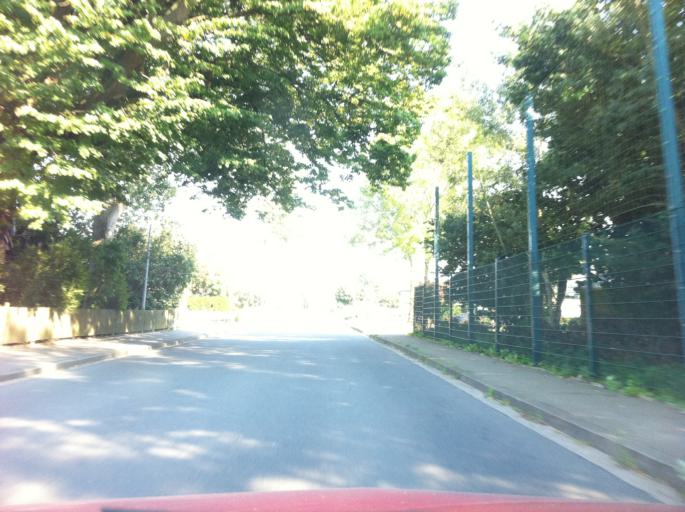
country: DE
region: Schleswig-Holstein
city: Harmsdorf
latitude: 54.3030
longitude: 10.8472
